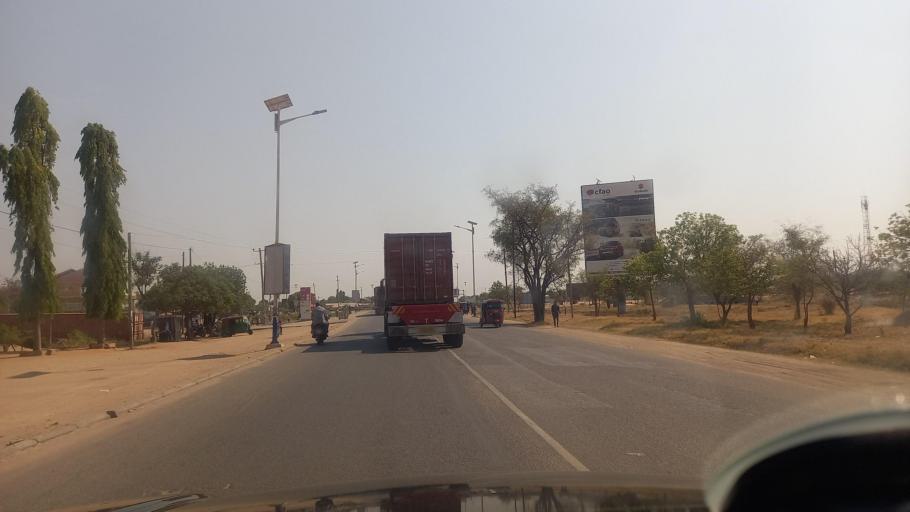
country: TZ
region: Dodoma
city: Dodoma
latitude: -6.1758
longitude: 35.7617
